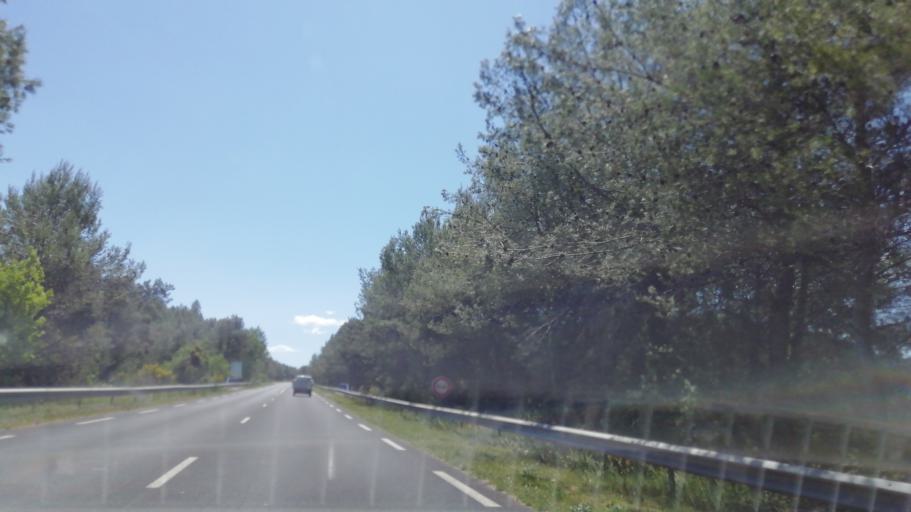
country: FR
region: Languedoc-Roussillon
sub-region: Departement de l'Herault
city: Saint-Clement-de-Riviere
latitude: 43.6802
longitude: 3.8212
